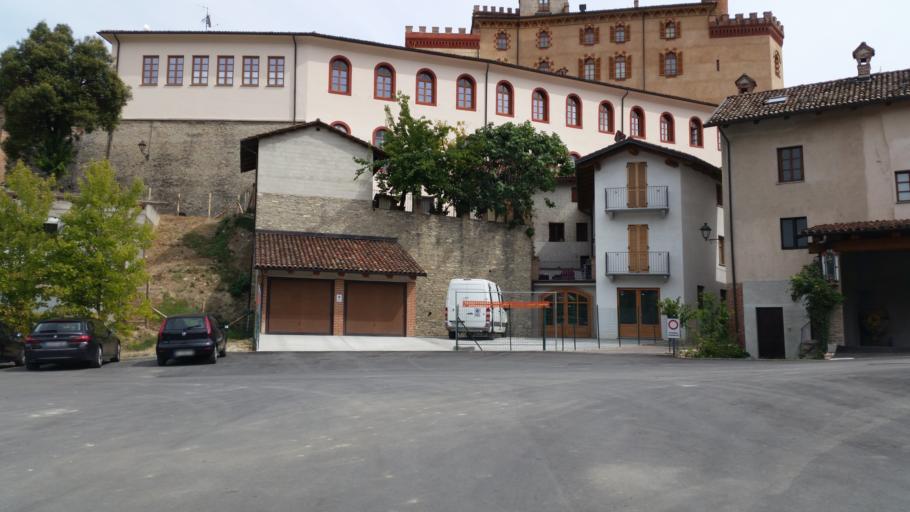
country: IT
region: Piedmont
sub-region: Provincia di Cuneo
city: Barolo
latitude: 44.6115
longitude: 7.9432
